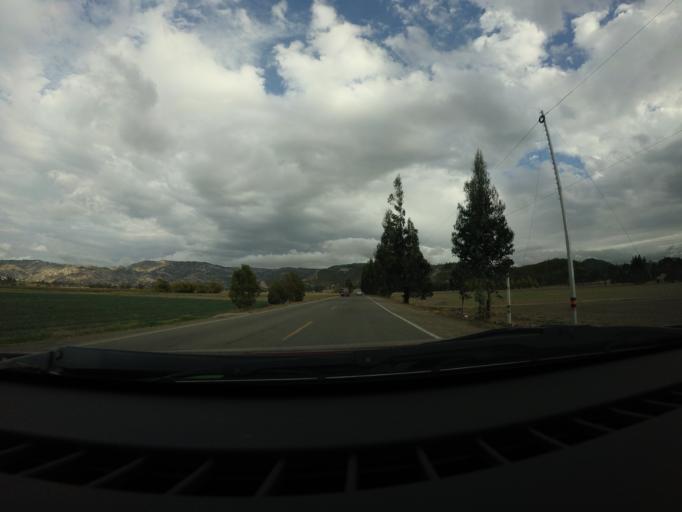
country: CO
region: Boyaca
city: Cucaita
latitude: 5.5436
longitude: -73.4828
